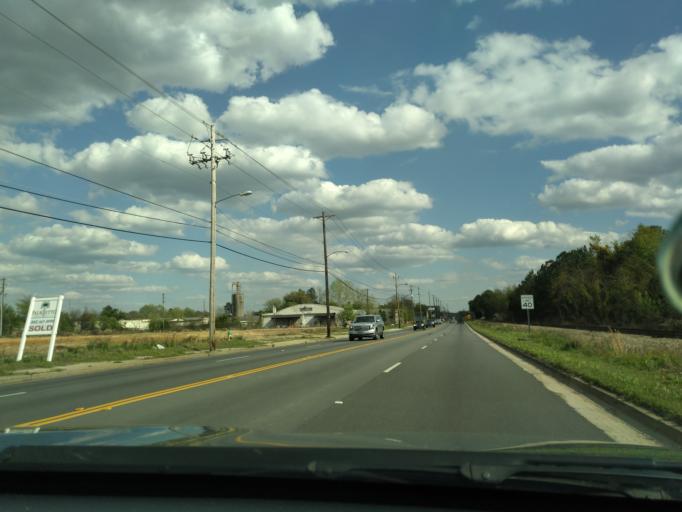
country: US
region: South Carolina
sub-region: Florence County
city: Florence
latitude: 34.2106
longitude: -79.7759
